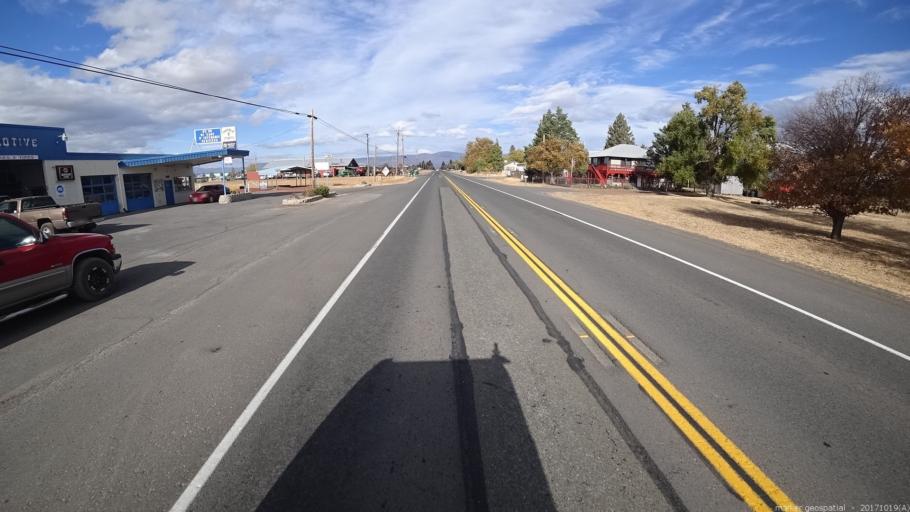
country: US
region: California
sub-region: Shasta County
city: Burney
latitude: 41.0167
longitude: -121.4312
